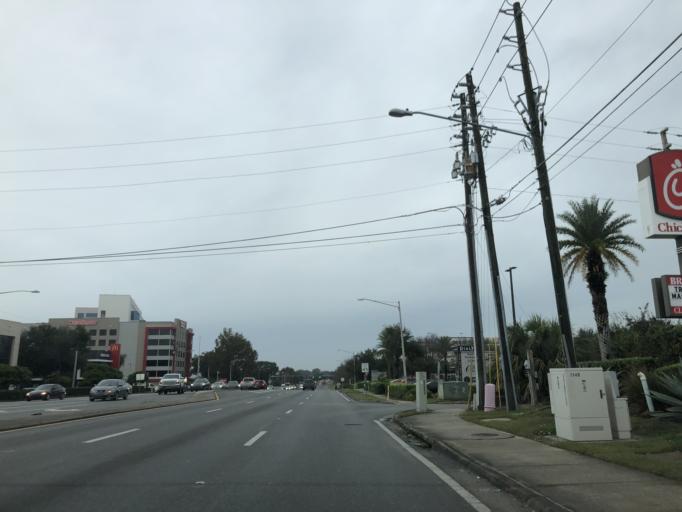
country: US
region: Florida
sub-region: Orange County
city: Doctor Phillips
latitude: 28.4501
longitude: -81.4788
